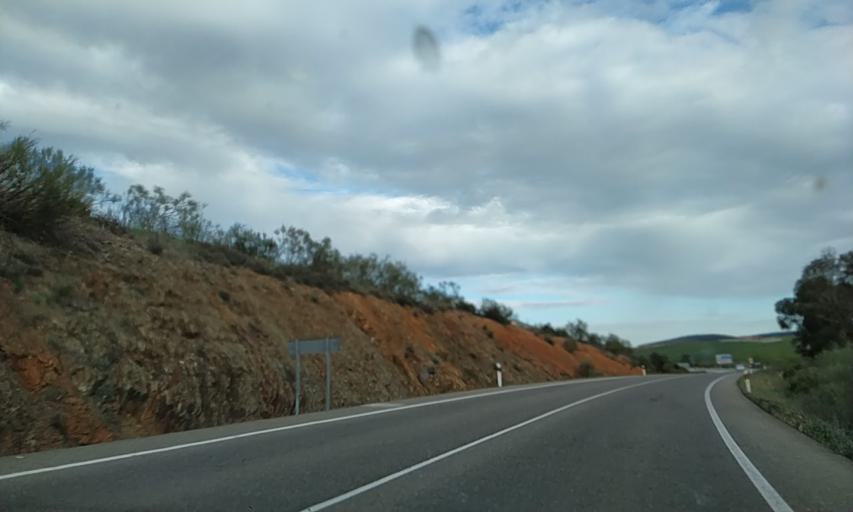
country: ES
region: Extremadura
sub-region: Provincia de Caceres
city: Pedroso de Acim
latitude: 39.8438
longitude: -6.4048
